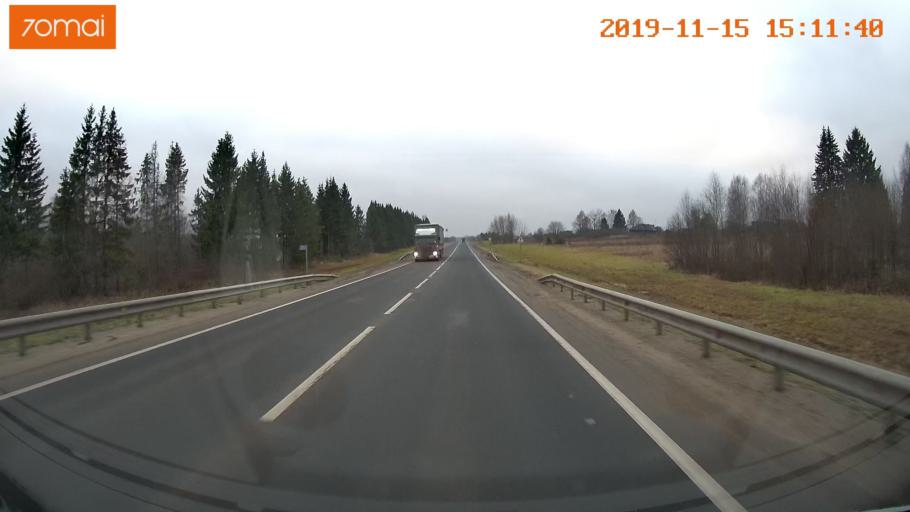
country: RU
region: Jaroslavl
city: Prechistoye
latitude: 58.3337
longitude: 40.2377
